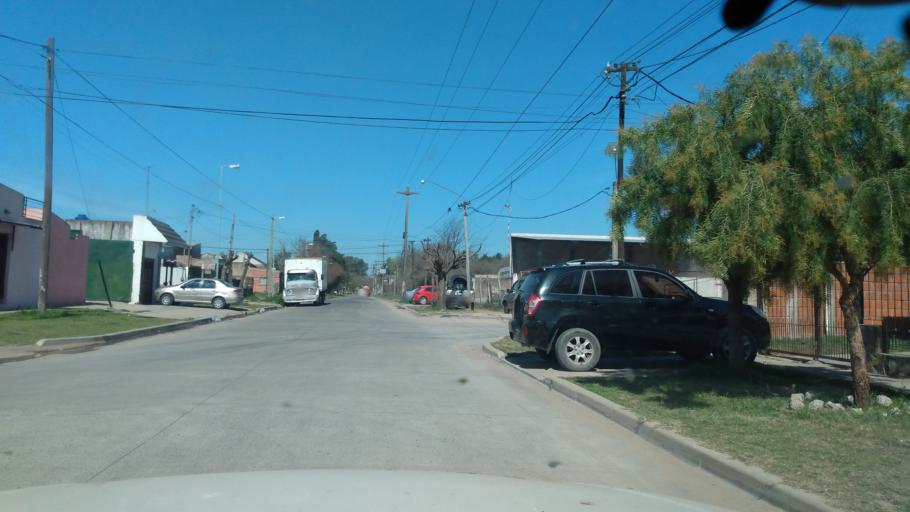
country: AR
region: Buenos Aires
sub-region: Partido de Lujan
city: Lujan
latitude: -34.5796
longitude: -59.1241
